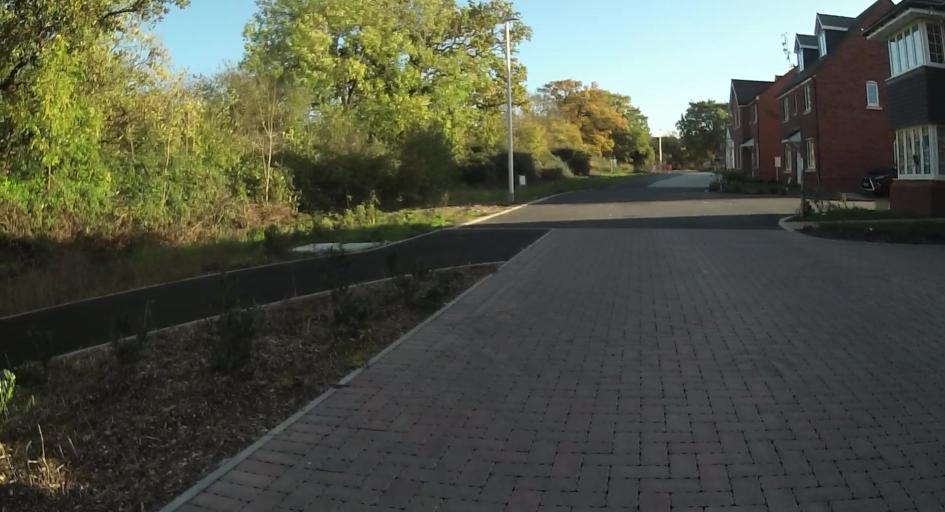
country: GB
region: England
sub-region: Wokingham
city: Winnersh
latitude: 51.4291
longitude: -0.8876
